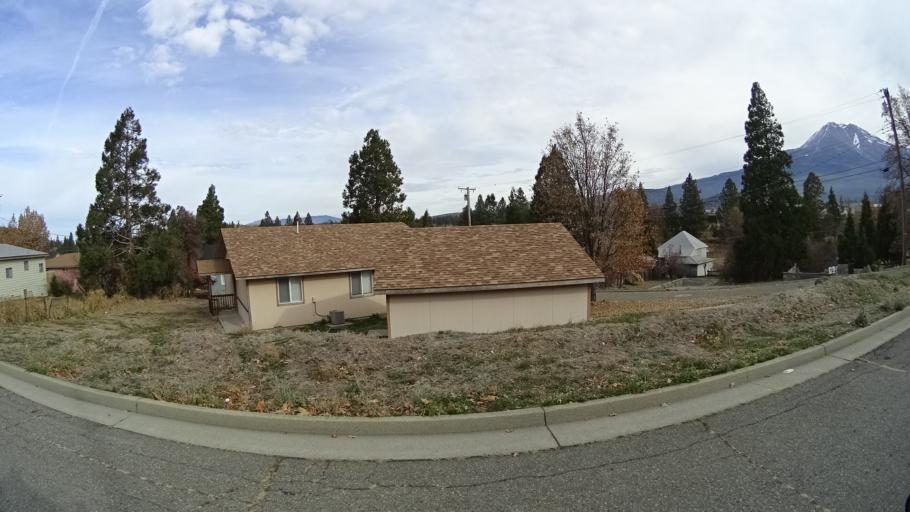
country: US
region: California
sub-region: Siskiyou County
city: Weed
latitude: 41.4345
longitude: -122.3861
